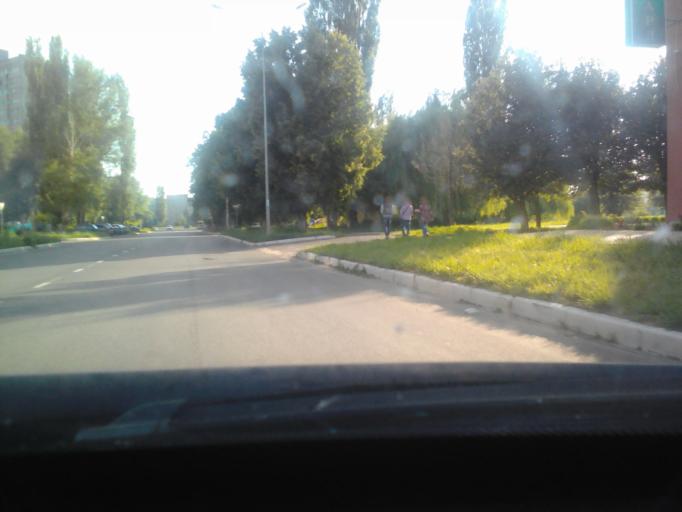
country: RU
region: Kursk
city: Kurchatov
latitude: 51.6586
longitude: 35.6695
